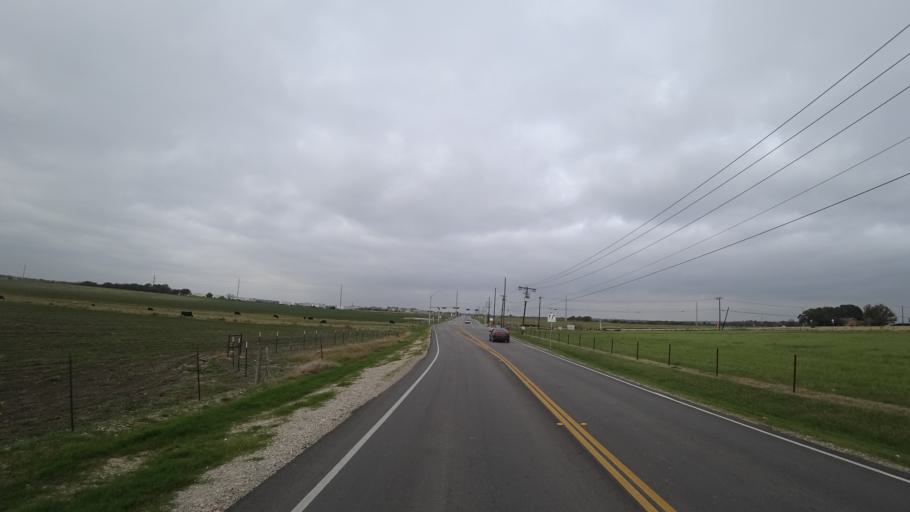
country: US
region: Texas
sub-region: Travis County
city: Pflugerville
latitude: 30.4189
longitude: -97.5780
